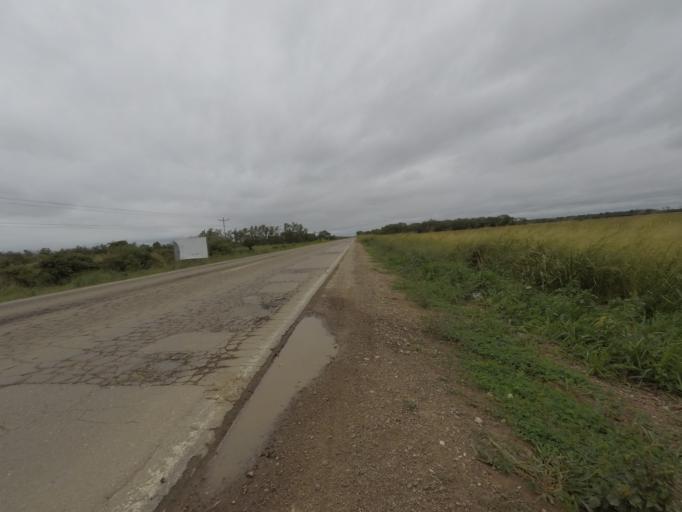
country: BO
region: Santa Cruz
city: Okinawa Numero Uno
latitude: -17.2989
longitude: -62.5553
